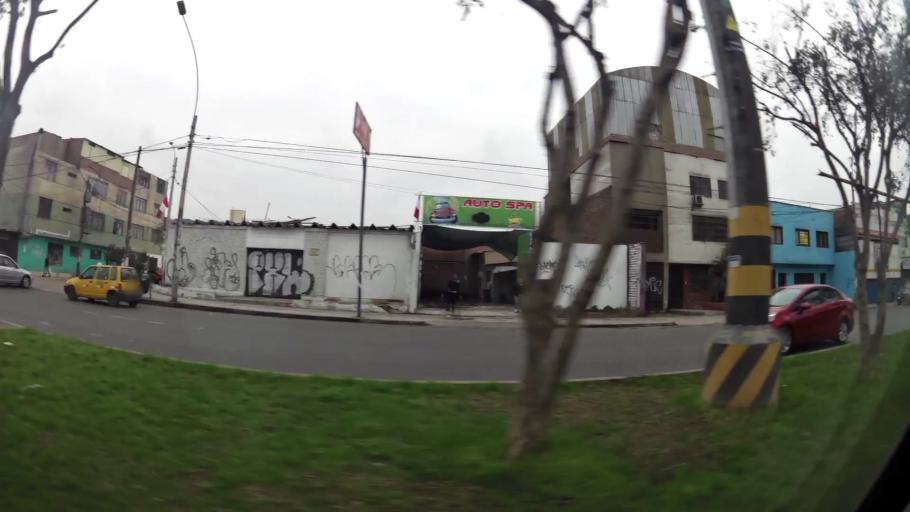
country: PE
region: Lima
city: Lima
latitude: -12.0509
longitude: -77.0603
